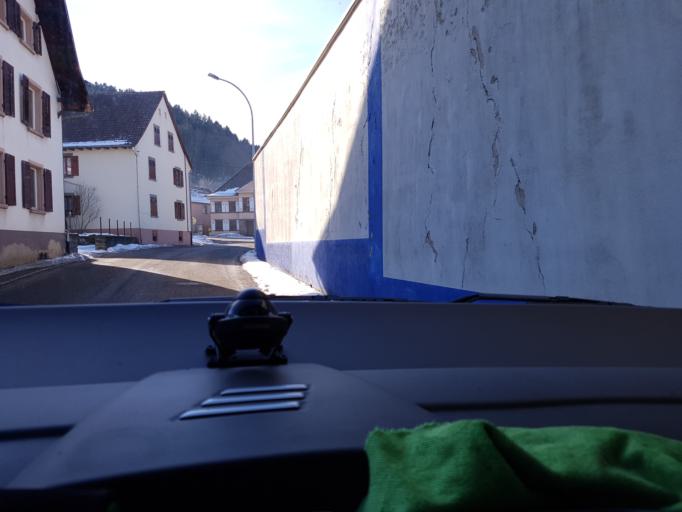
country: FR
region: Alsace
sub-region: Departement du Haut-Rhin
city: Metzeral
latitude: 47.9988
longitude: 7.0745
